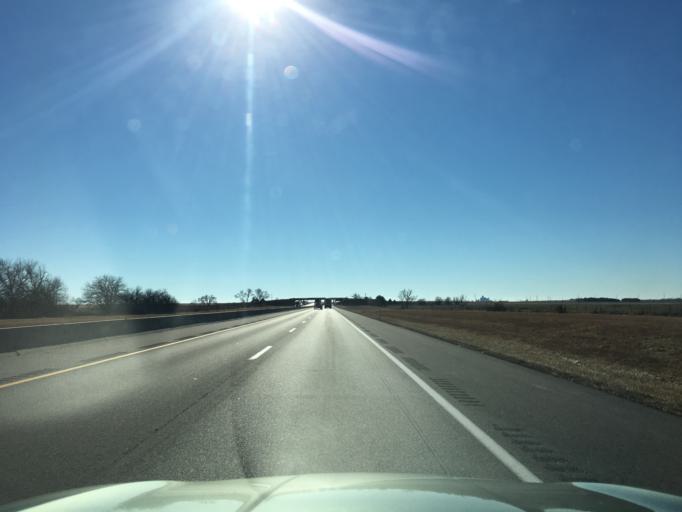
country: US
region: Kansas
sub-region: Sumner County
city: Wellington
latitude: 37.3098
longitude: -97.3406
